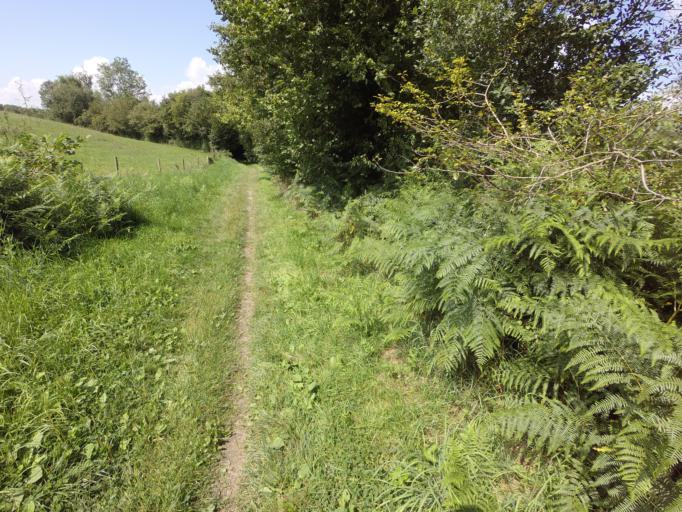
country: BE
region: Wallonia
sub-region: Province de Liege
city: Lontzen
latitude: 50.6931
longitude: 6.0004
